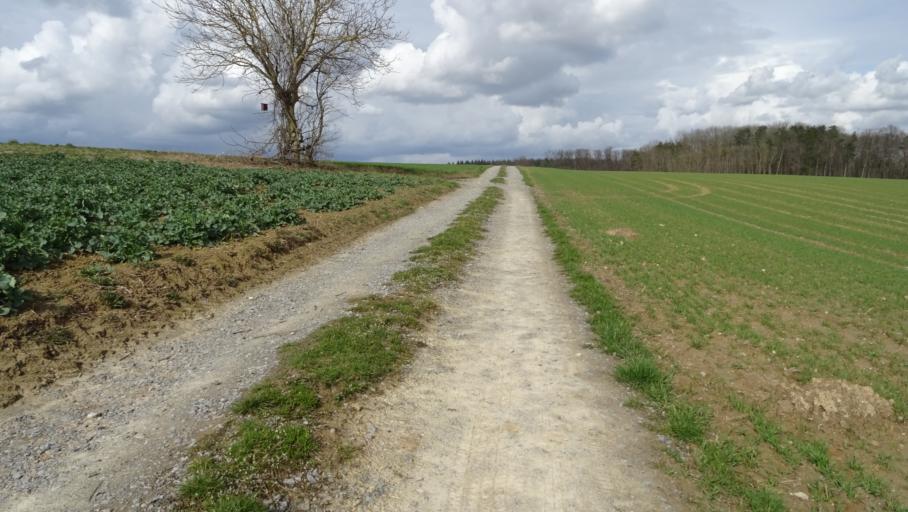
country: DE
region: Baden-Wuerttemberg
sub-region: Karlsruhe Region
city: Limbach
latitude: 49.4310
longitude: 9.2602
